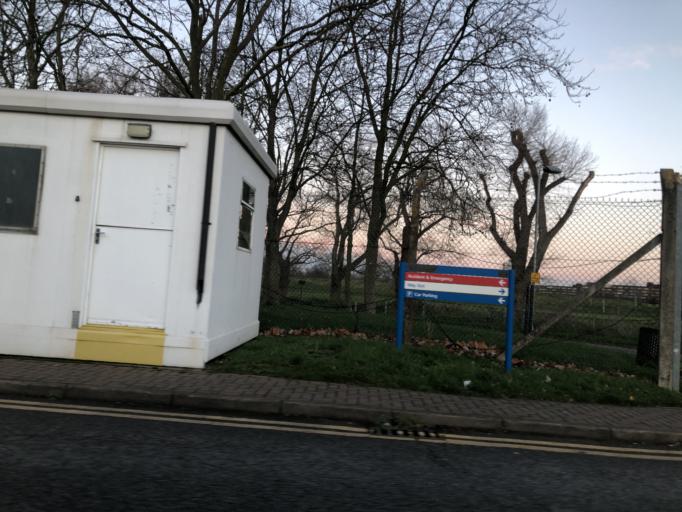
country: GB
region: England
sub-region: Greater London
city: Woolwich
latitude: 51.4791
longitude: 0.0522
